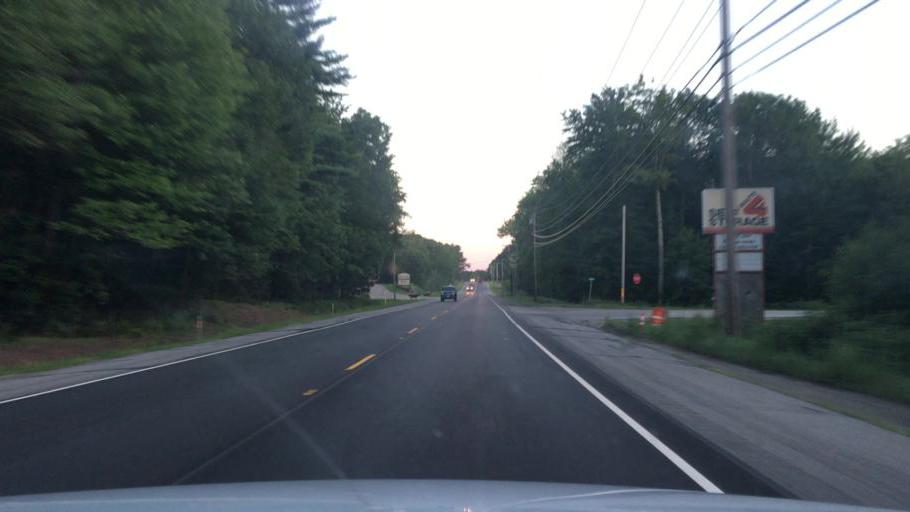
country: US
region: Maine
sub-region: Androscoggin County
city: Turner
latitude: 44.2118
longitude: -70.2460
